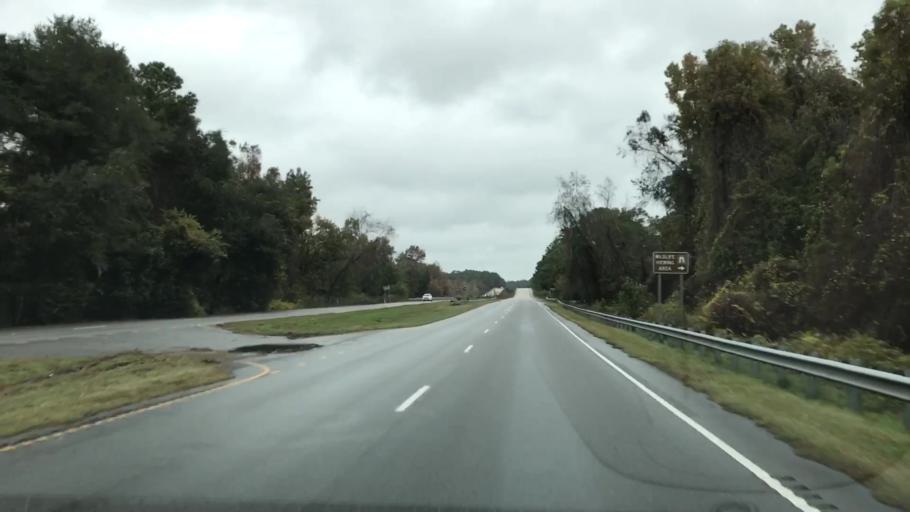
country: US
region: South Carolina
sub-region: Georgetown County
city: Georgetown
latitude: 33.2038
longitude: -79.3887
